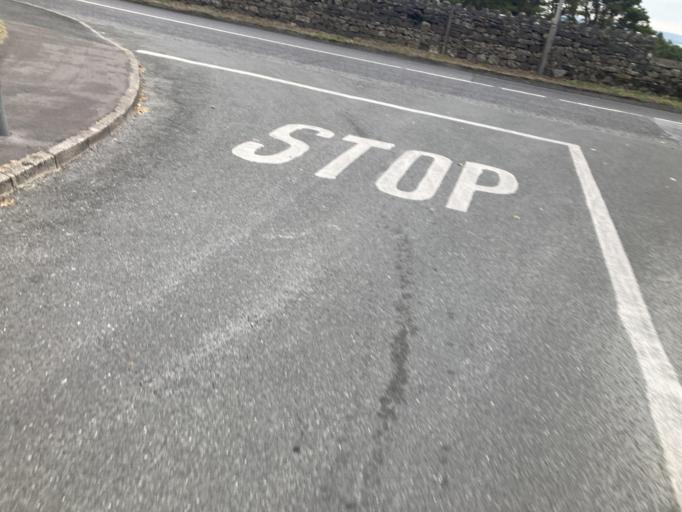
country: IE
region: Connaught
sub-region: County Galway
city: Gaillimh
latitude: 53.2668
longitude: -9.0940
